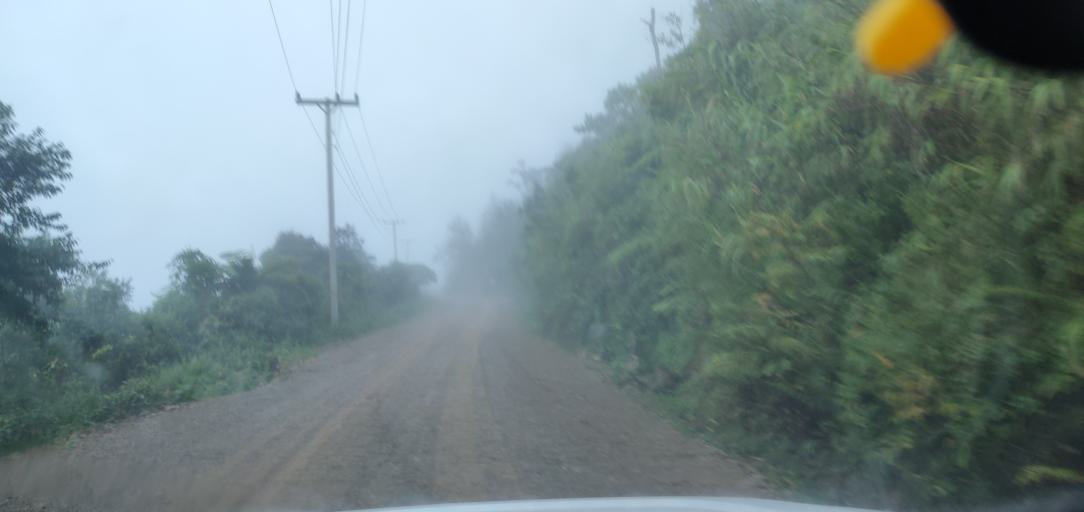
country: LA
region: Phongsali
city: Phongsali
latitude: 21.3985
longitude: 102.1912
